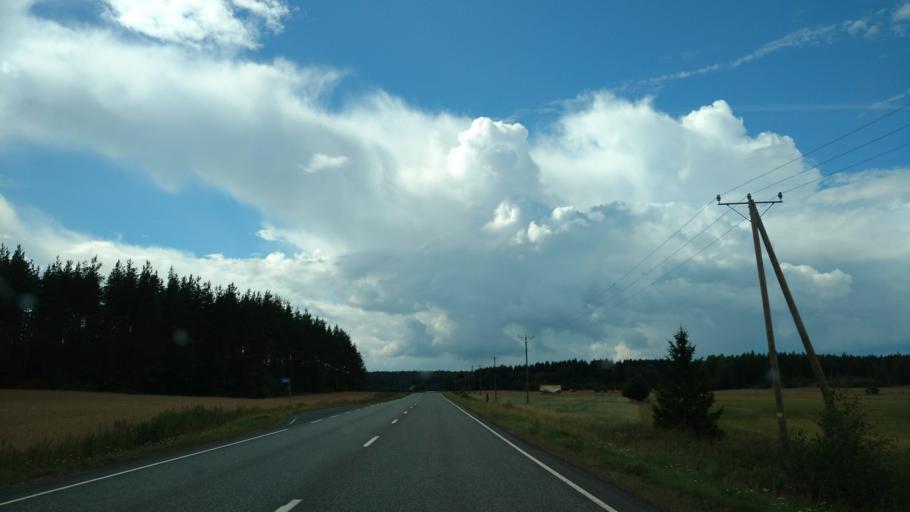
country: FI
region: Varsinais-Suomi
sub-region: Turku
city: Sauvo
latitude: 60.4065
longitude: 22.8079
